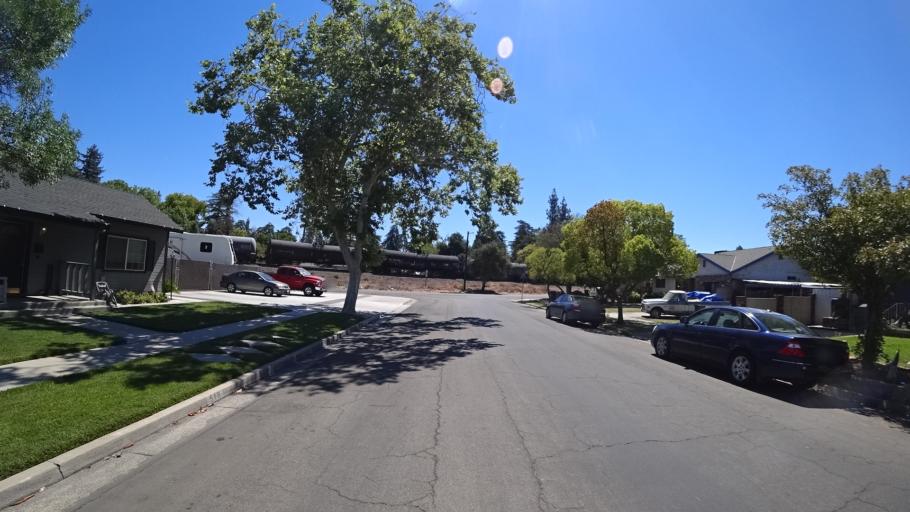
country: US
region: California
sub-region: Fresno County
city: Fresno
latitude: 36.7831
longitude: -119.8060
